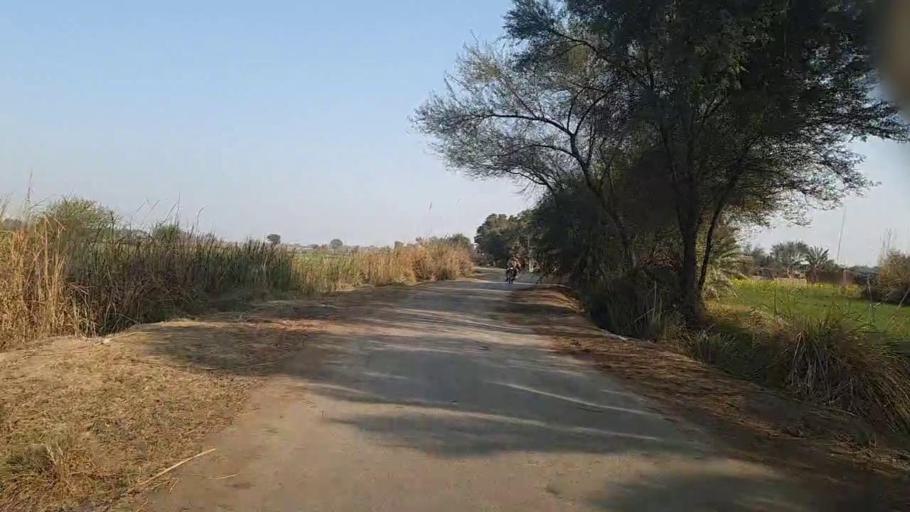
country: PK
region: Sindh
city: Mirpur Mathelo
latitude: 27.8758
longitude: 69.6224
